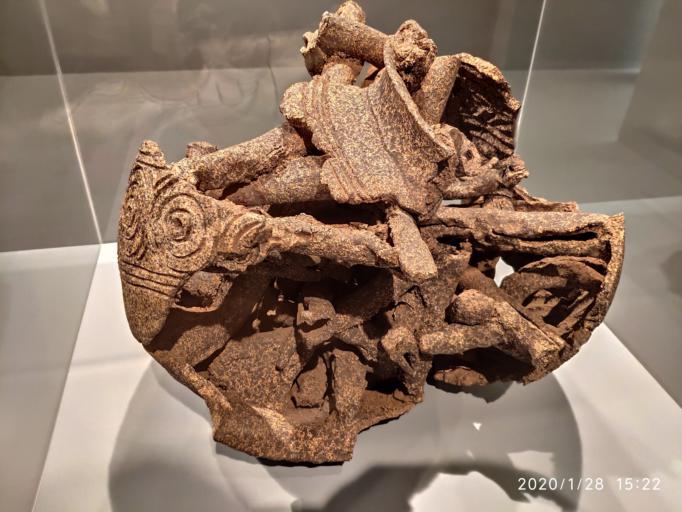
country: QA
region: Baladiyat ar Rayyan
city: Ar Rayyan
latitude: 25.3136
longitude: 51.4242
